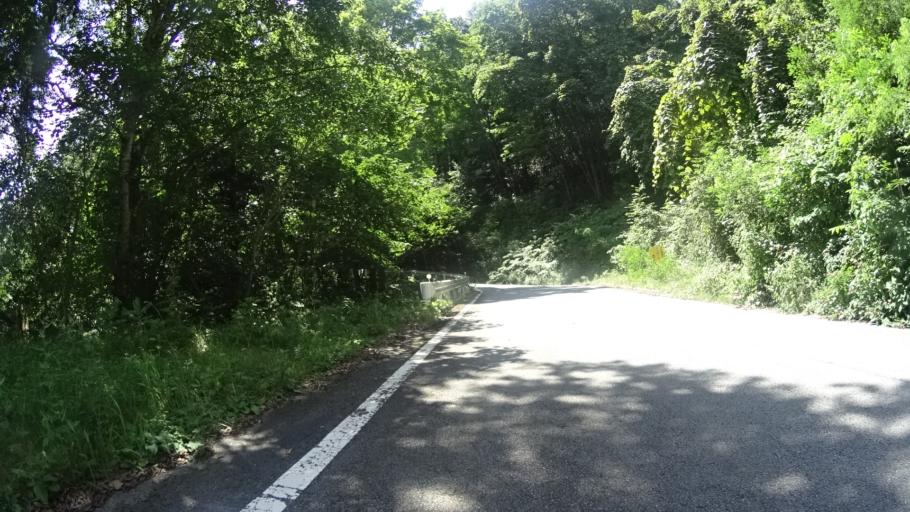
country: JP
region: Yamanashi
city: Enzan
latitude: 35.8203
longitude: 138.6521
